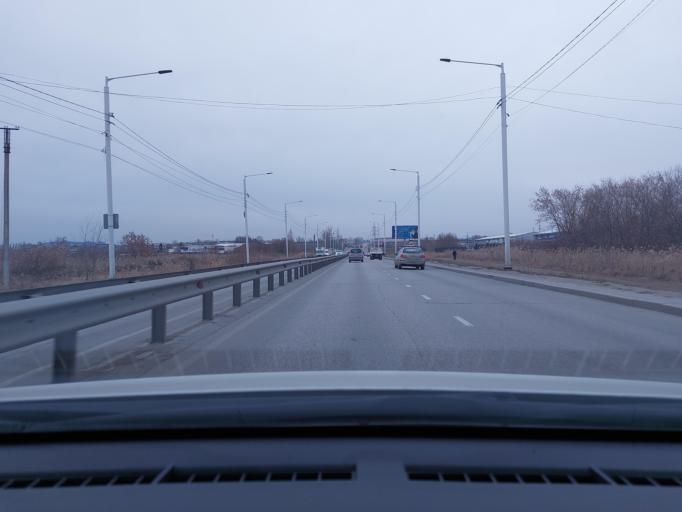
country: RU
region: Irkutsk
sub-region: Irkutskiy Rayon
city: Irkutsk
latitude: 52.3321
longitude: 104.2337
